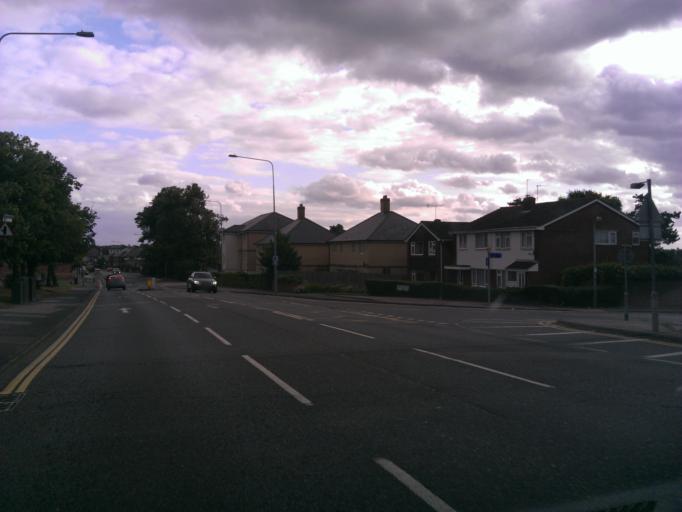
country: GB
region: England
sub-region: Essex
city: Colchester
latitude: 51.8979
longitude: 0.9199
